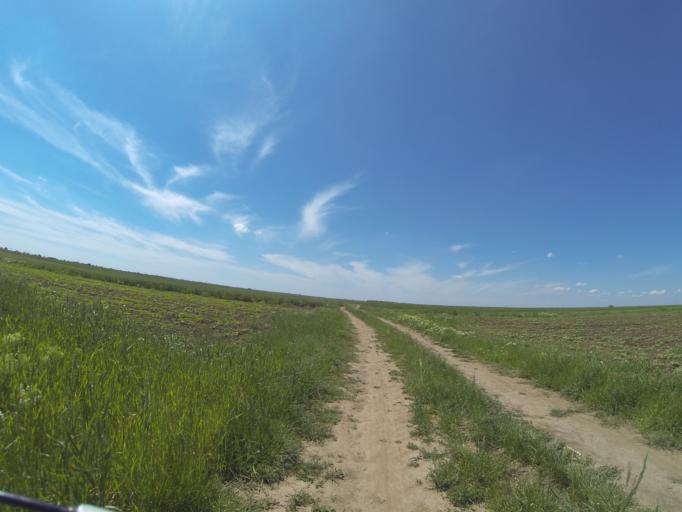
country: RO
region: Dolj
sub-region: Comuna Leu
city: Leu
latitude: 44.2172
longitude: 24.0170
